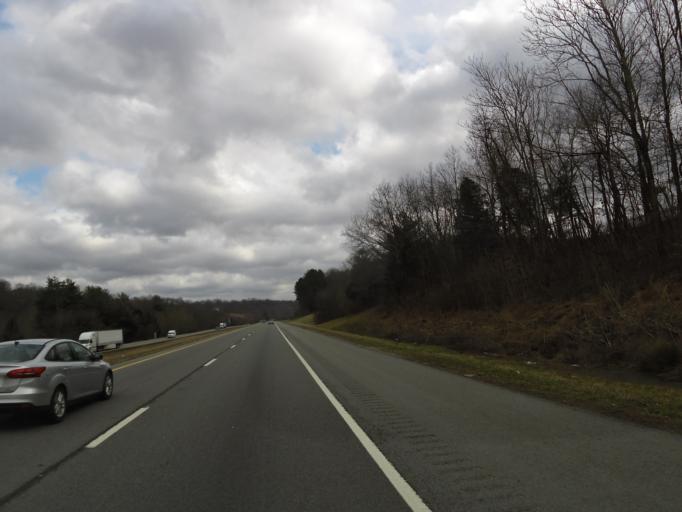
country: US
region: Tennessee
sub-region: Coffee County
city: New Union
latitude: 35.5653
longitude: -86.2179
